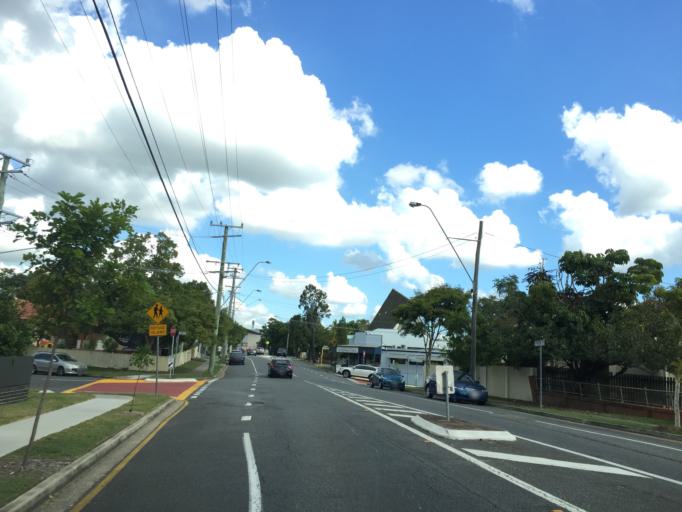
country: AU
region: Queensland
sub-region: Brisbane
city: Wilston
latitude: -27.4427
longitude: 152.9948
